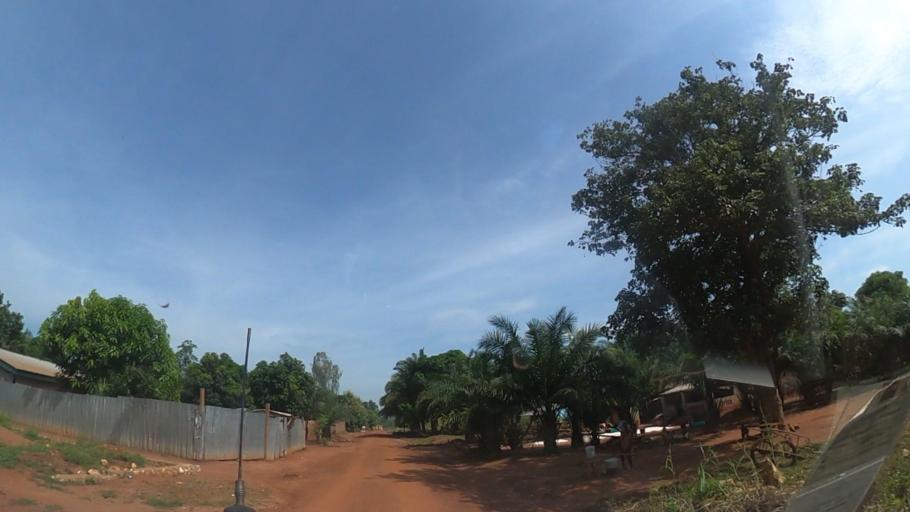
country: CF
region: Ombella-Mpoko
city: Bimbo
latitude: 4.3165
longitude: 18.4689
